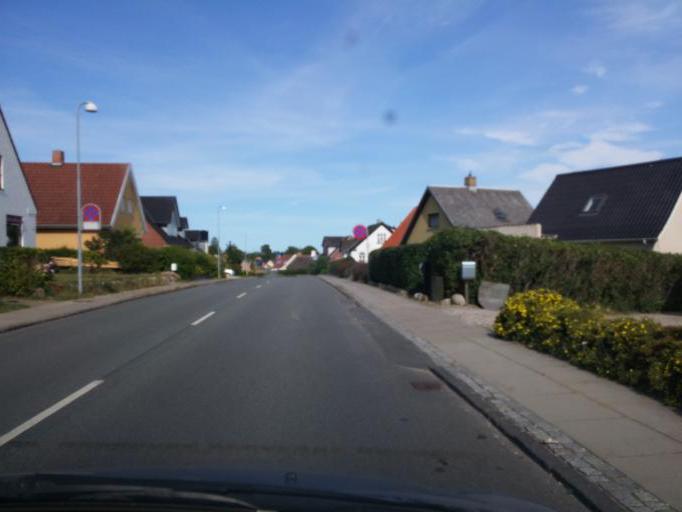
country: DK
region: South Denmark
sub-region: Kerteminde Kommune
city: Munkebo
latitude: 55.4548
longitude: 10.5517
